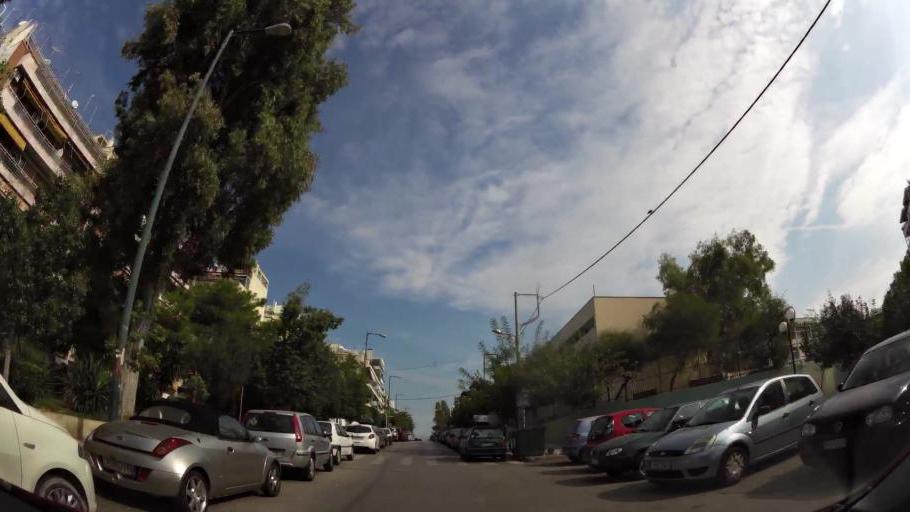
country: GR
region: Attica
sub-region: Nomarchia Athinas
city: Nea Smyrni
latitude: 37.9489
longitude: 23.7123
